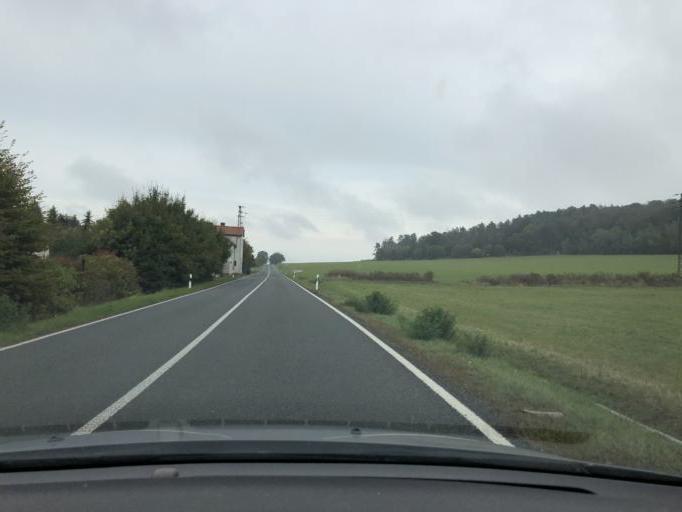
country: DE
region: Thuringia
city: Auleben
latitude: 51.3902
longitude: 10.9290
